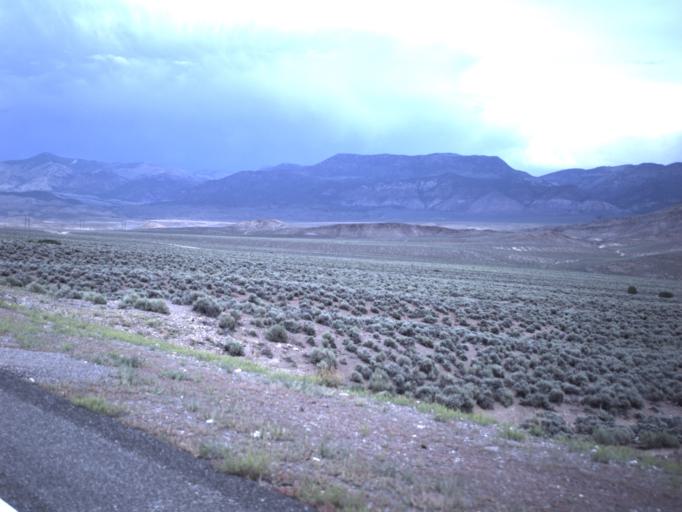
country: US
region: Utah
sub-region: Piute County
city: Junction
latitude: 38.3199
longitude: -112.2202
